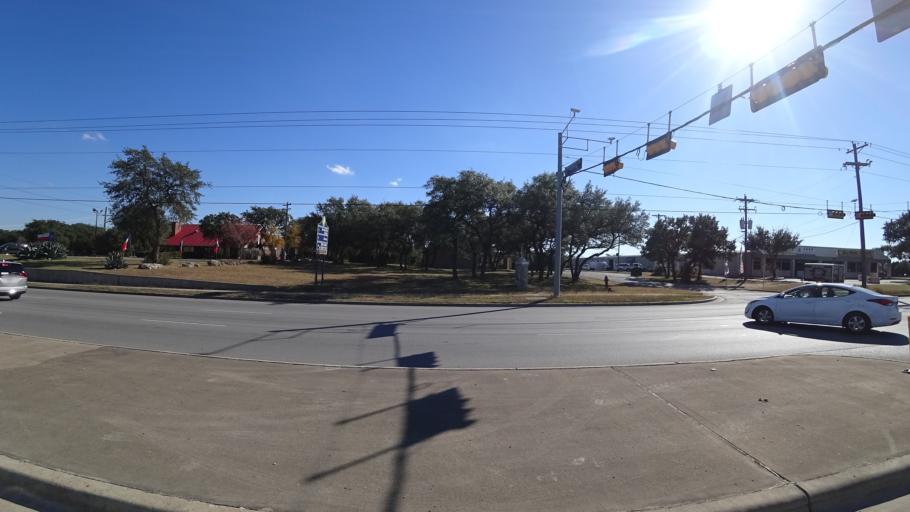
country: US
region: Texas
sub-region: Williamson County
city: Cedar Park
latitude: 30.5199
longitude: -97.8333
